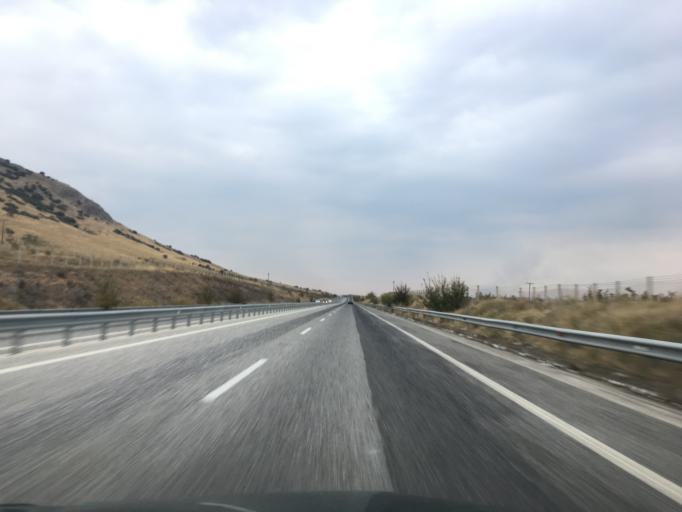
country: GR
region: Thessaly
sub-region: Trikala
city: Zarkos
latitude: 39.5970
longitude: 22.1911
